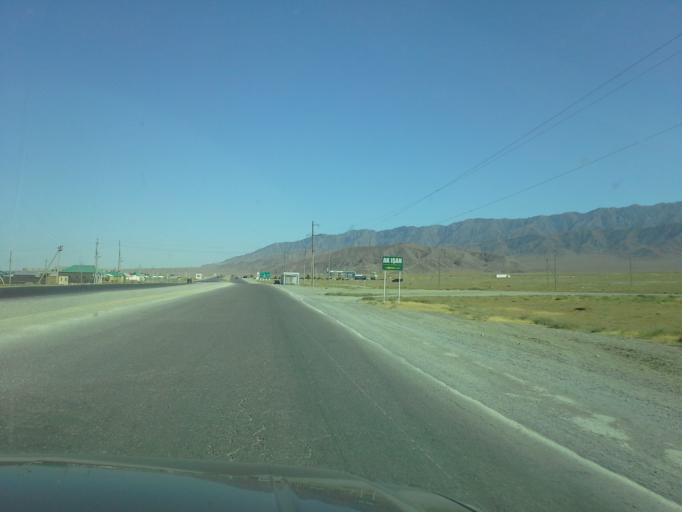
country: TM
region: Ahal
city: Baharly
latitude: 38.5424
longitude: 57.1501
